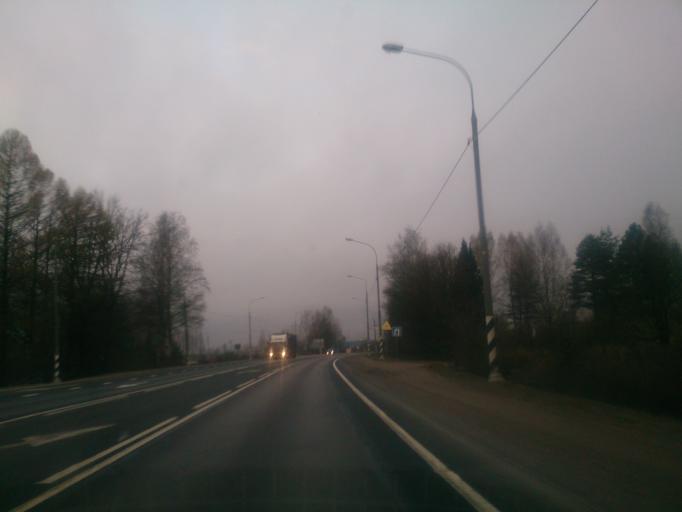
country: RU
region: Novgorod
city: Valday
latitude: 58.0313
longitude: 32.9769
